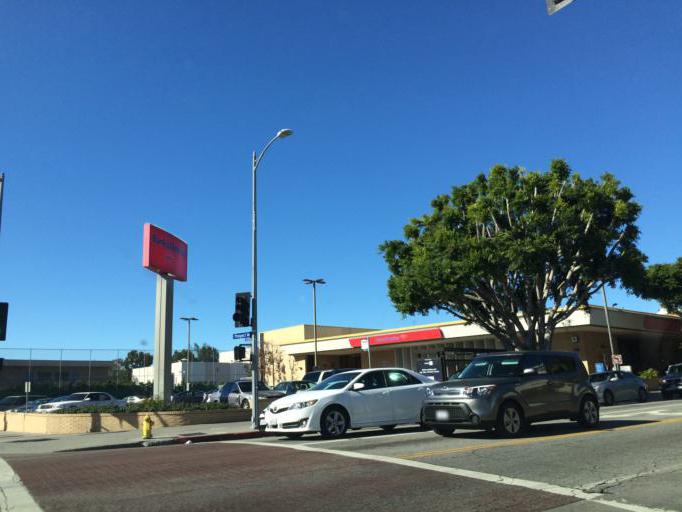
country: US
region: California
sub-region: Los Angeles County
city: Silver Lake
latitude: 34.1018
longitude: -118.2917
